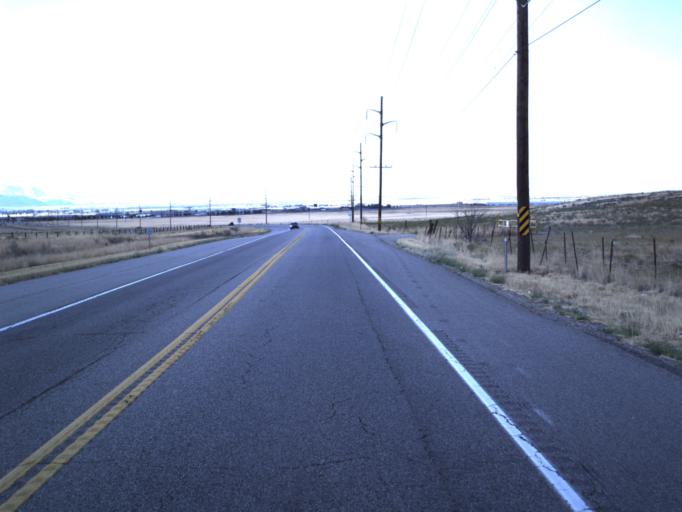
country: US
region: Utah
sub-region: Tooele County
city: Tooele
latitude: 40.5582
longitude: -112.3509
